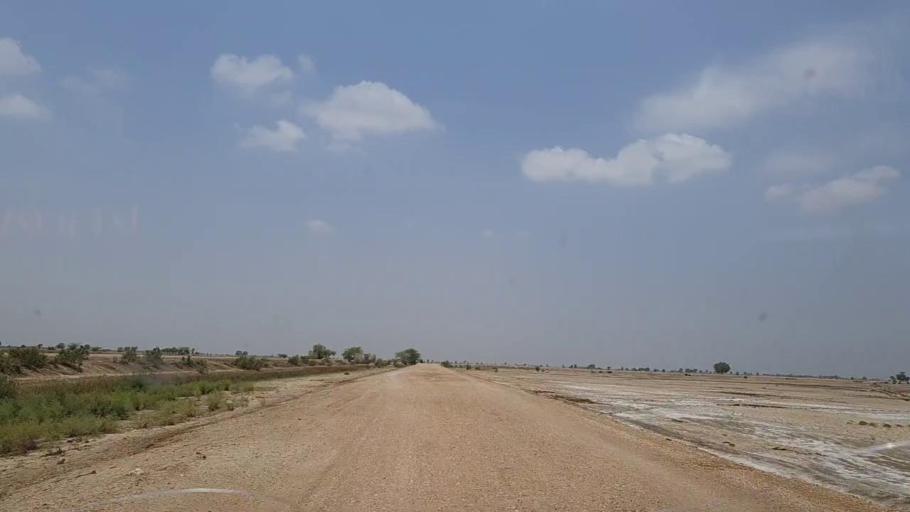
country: PK
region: Sindh
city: Johi
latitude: 26.7635
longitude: 67.6622
